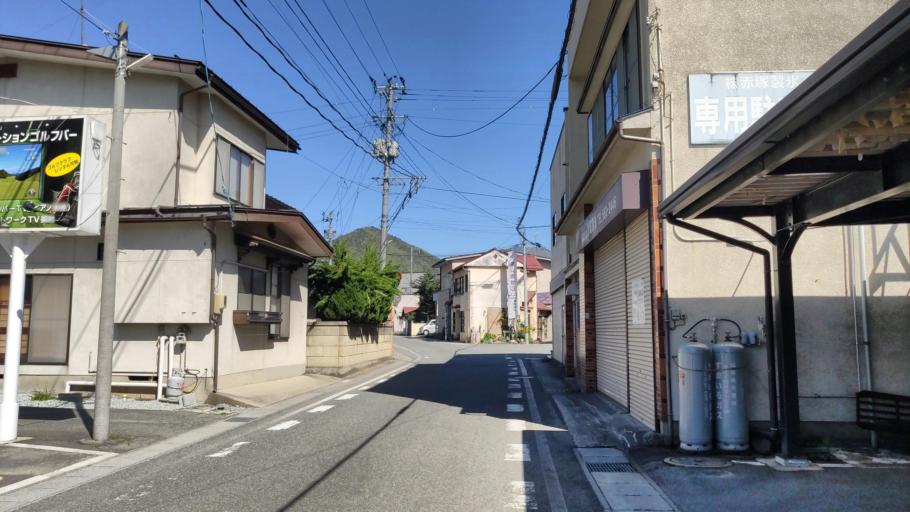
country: JP
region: Yamagata
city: Tendo
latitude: 38.3593
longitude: 140.3743
